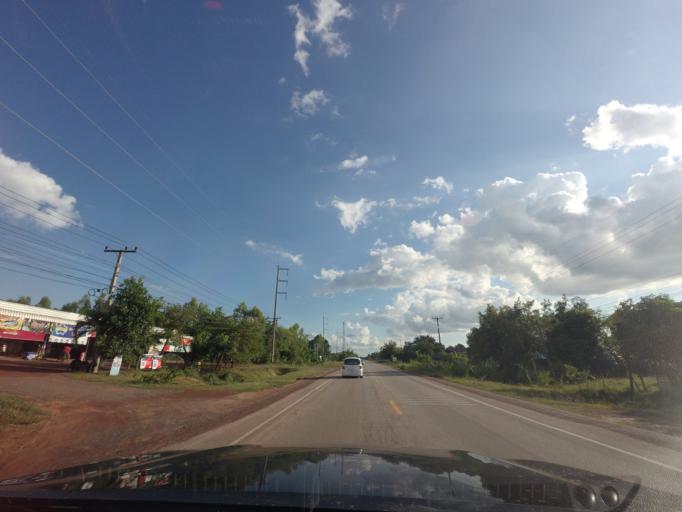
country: TH
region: Changwat Udon Thani
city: Thung Fon
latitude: 17.4858
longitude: 103.1965
